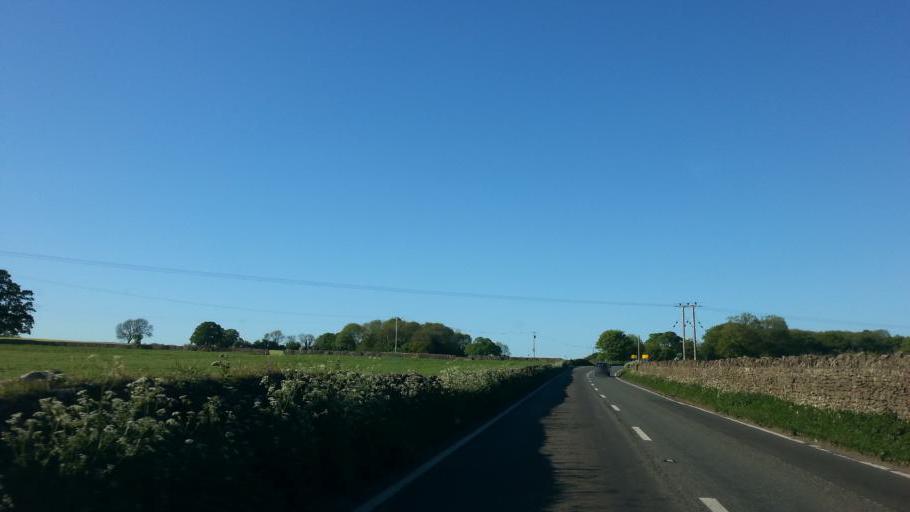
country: GB
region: England
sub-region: Bath and North East Somerset
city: Cameley
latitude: 51.2883
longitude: -2.5427
